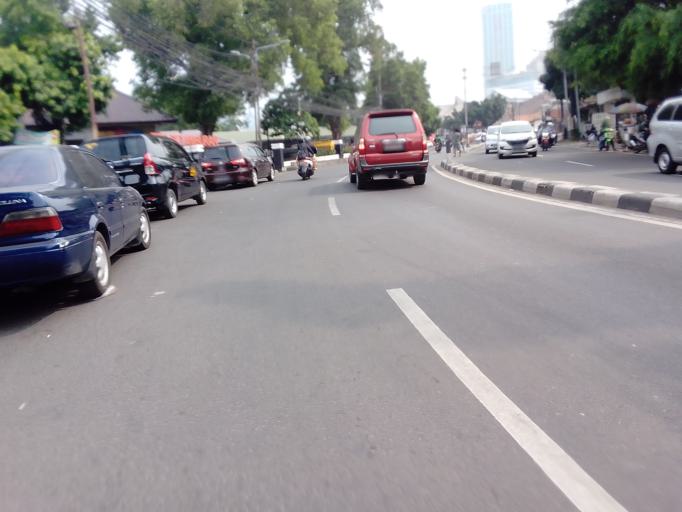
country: ID
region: Jakarta Raya
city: Jakarta
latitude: -6.1974
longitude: 106.8043
